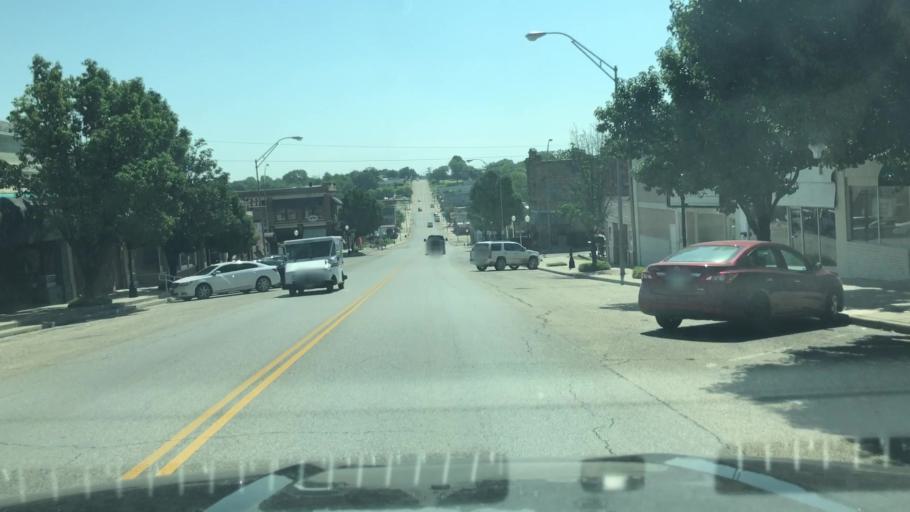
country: US
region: Oklahoma
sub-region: Creek County
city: Drumright
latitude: 35.9885
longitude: -96.6006
